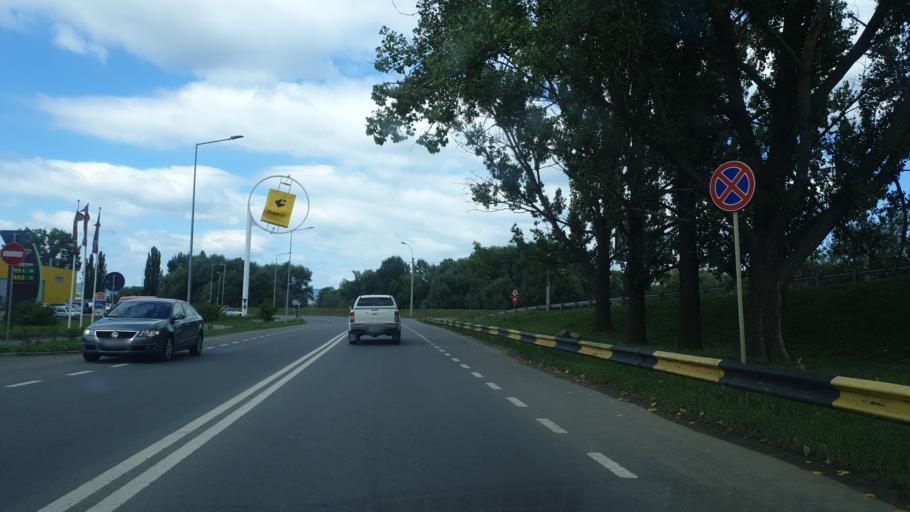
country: RO
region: Covasna
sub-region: Municipiul Sfantu Gheorghe
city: Sfantu-Gheorghe
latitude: 45.8637
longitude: 25.8035
